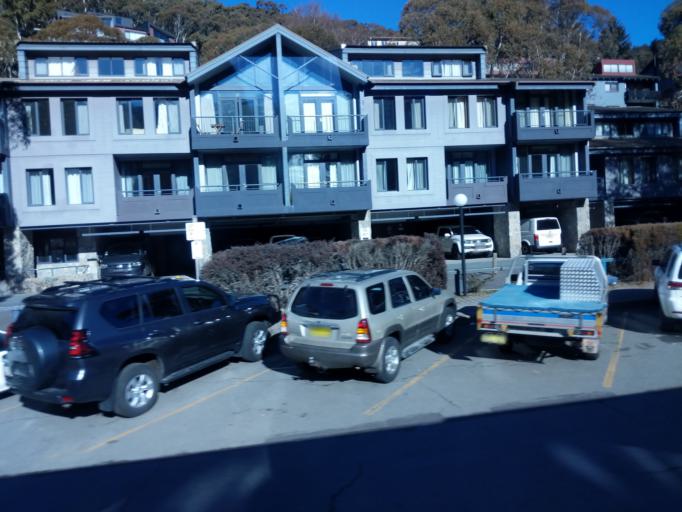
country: AU
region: New South Wales
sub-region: Snowy River
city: Jindabyne
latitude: -36.5035
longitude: 148.3064
